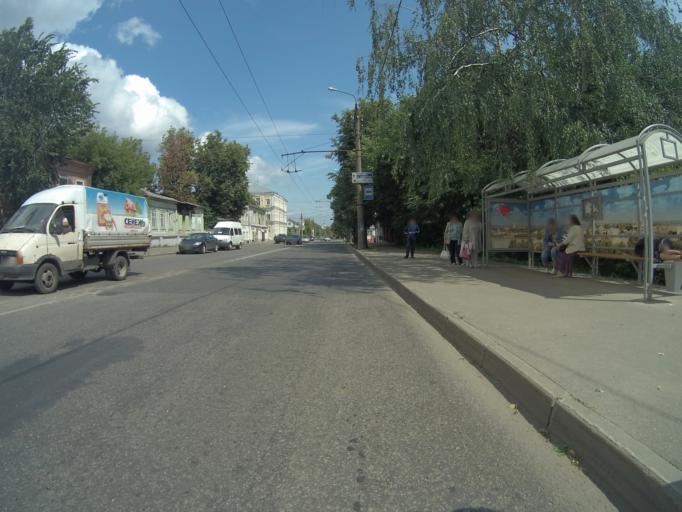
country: RU
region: Vladimir
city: Vladimir
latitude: 56.1353
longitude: 40.4073
